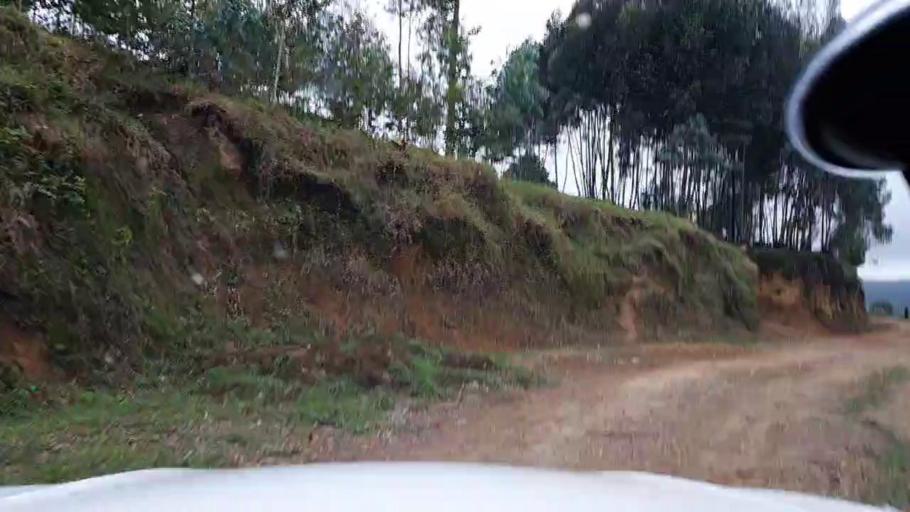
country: RW
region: Western Province
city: Kibuye
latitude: -2.0836
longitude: 29.5056
